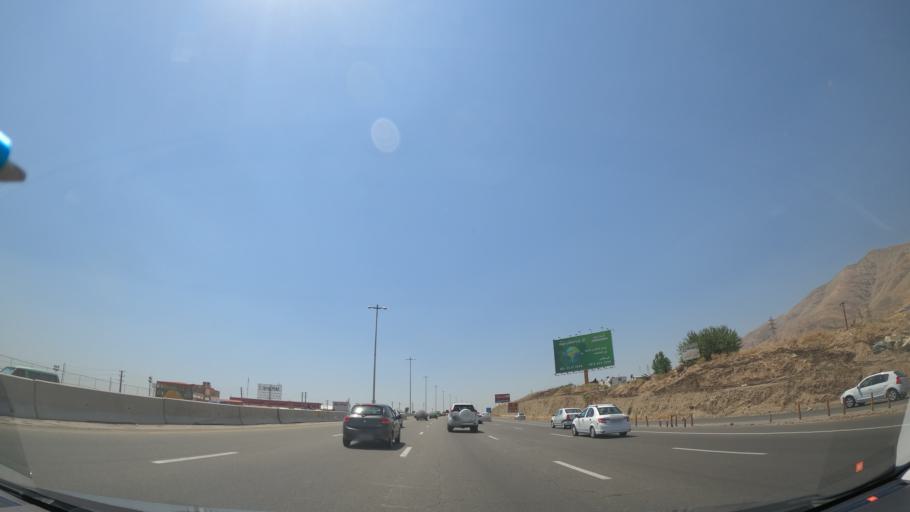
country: IR
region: Tehran
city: Shahr-e Qods
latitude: 35.7458
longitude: 51.0897
